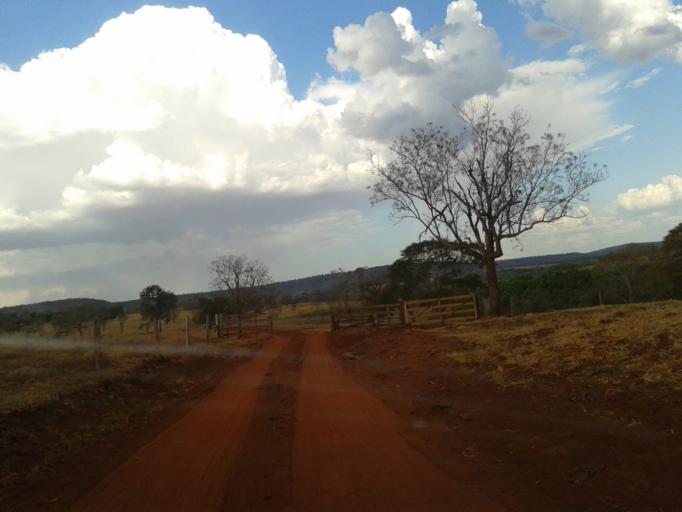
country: BR
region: Minas Gerais
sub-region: Santa Vitoria
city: Santa Vitoria
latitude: -19.1704
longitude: -49.9498
